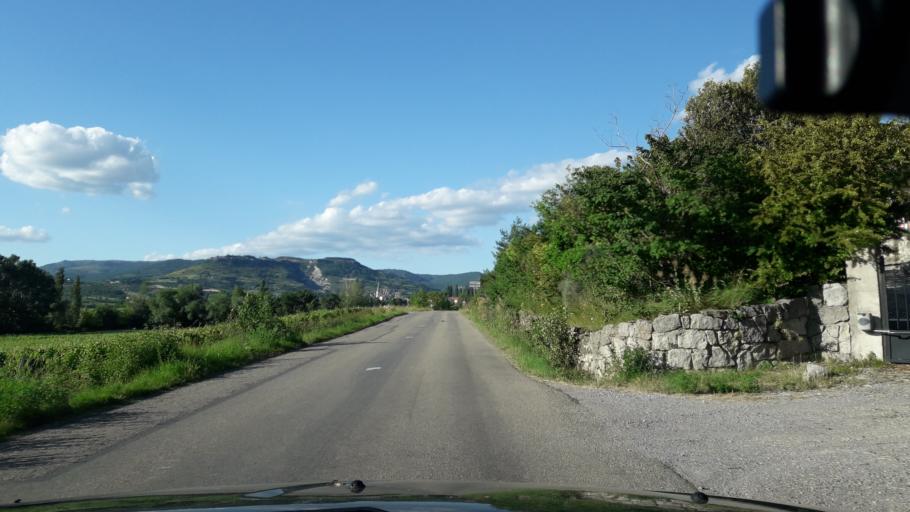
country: FR
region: Rhone-Alpes
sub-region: Departement de l'Ardeche
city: Lavilledieu
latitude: 44.6036
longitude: 4.4674
